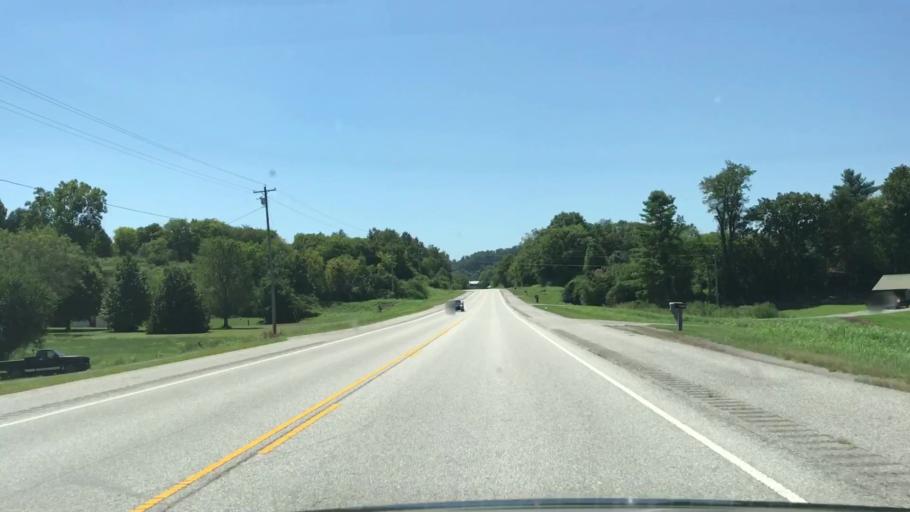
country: US
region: Tennessee
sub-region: Jackson County
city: Gainesboro
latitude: 36.4293
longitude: -85.6360
